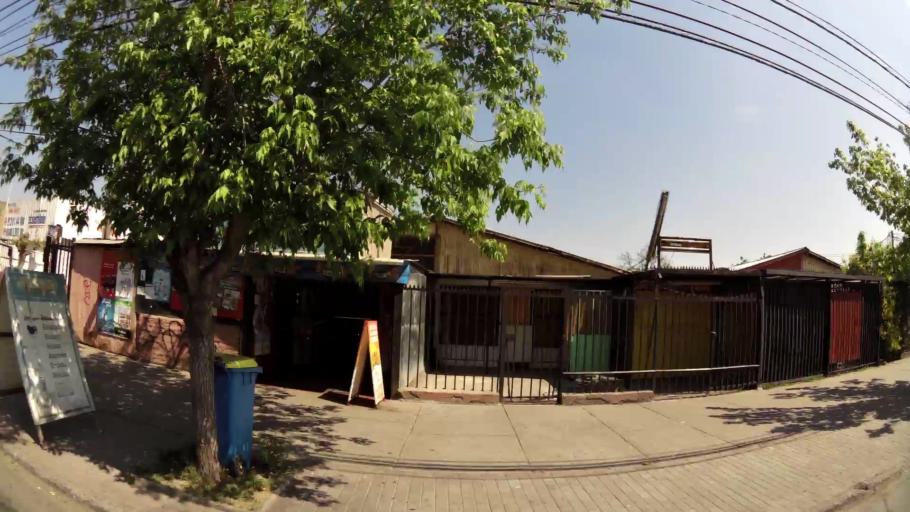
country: CL
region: Santiago Metropolitan
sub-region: Provincia de Santiago
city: La Pintana
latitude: -33.5570
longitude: -70.6066
